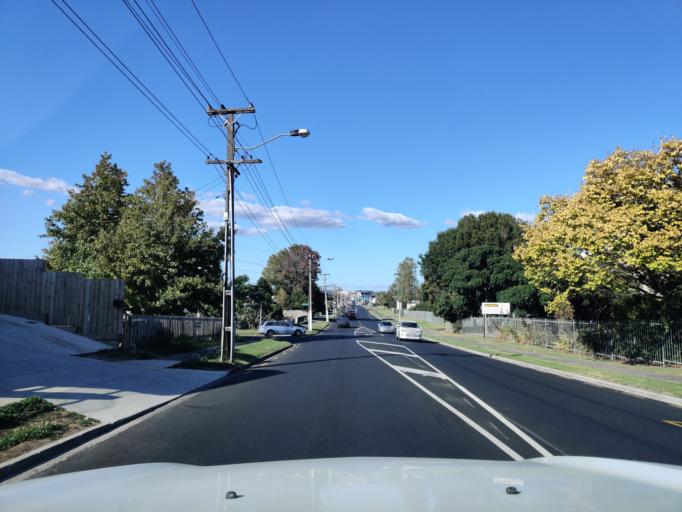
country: NZ
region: Auckland
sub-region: Auckland
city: Takanini
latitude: -37.0346
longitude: 174.9001
